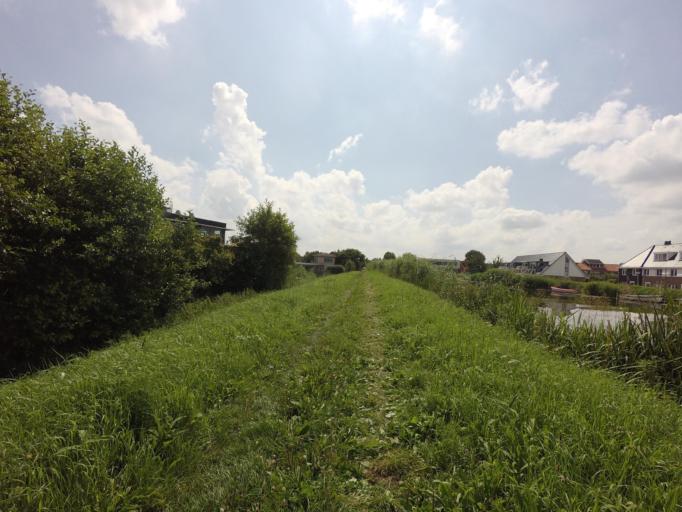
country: NL
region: South Holland
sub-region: Gemeente Vlist
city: Haastrecht
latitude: 52.0461
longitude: 4.8001
